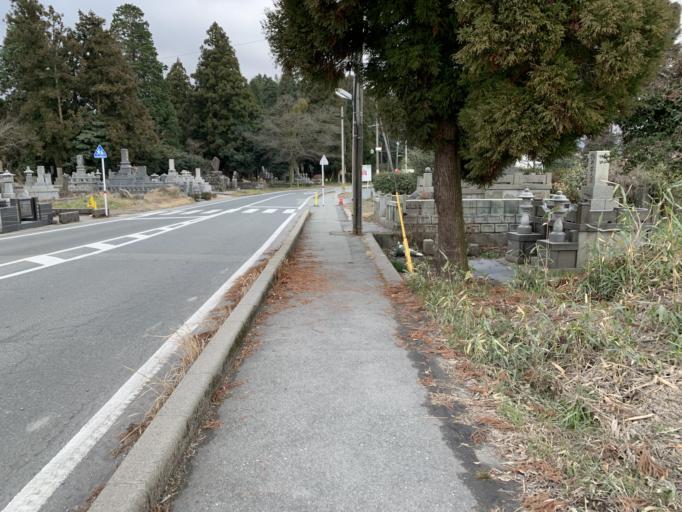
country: JP
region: Kumamoto
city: Aso
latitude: 32.9373
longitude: 131.1141
